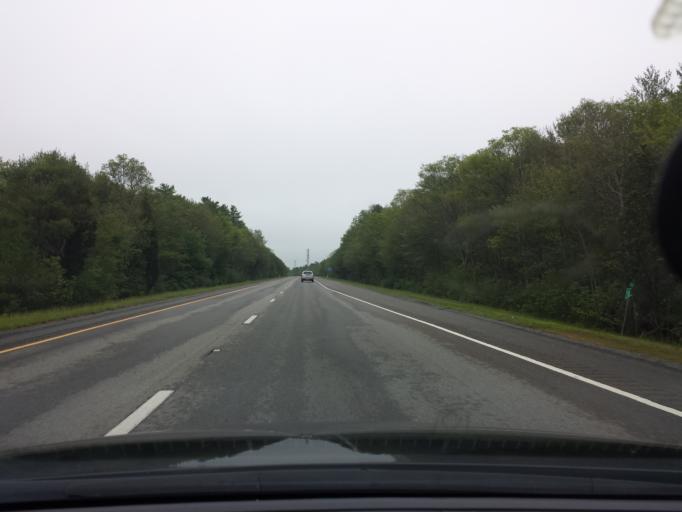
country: US
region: Massachusetts
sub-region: Plymouth County
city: Mattapoisett Center
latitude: 41.6799
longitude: -70.8162
